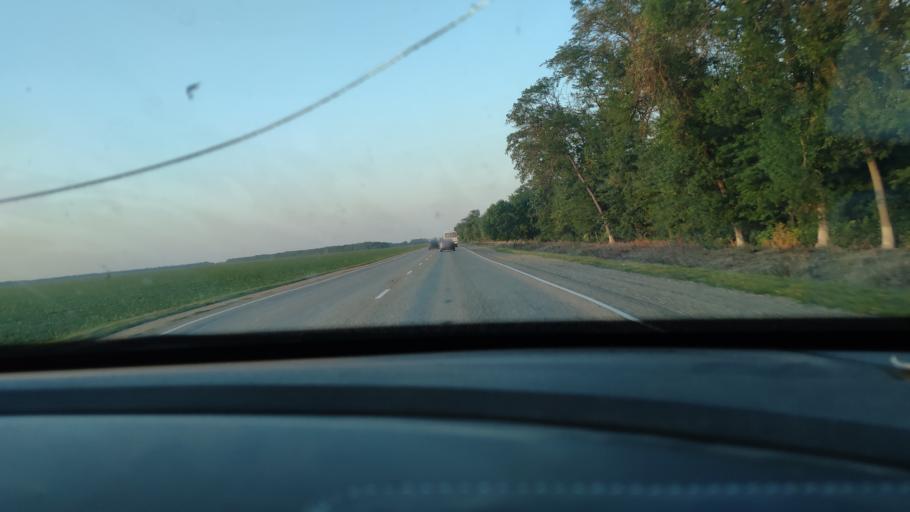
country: RU
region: Krasnodarskiy
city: Starominskaya
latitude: 46.4511
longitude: 39.0302
